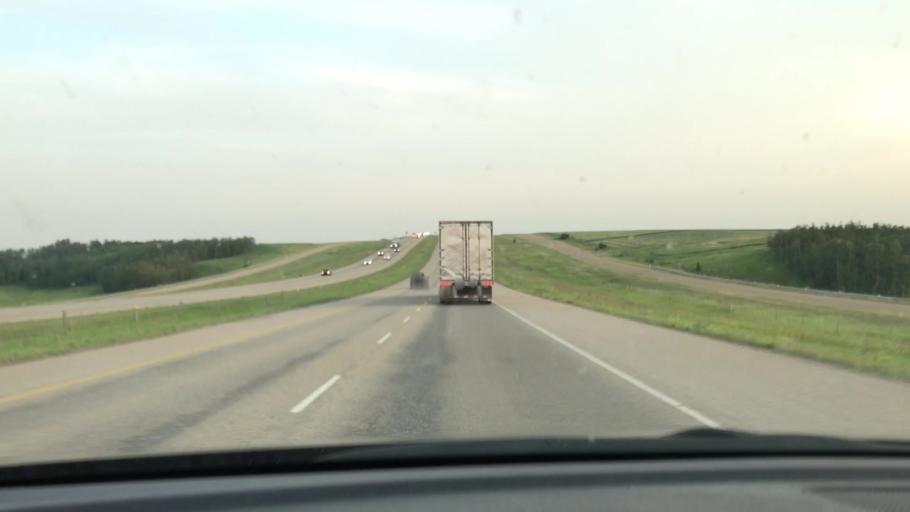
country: CA
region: Alberta
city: Carstairs
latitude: 51.5797
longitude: -114.0253
